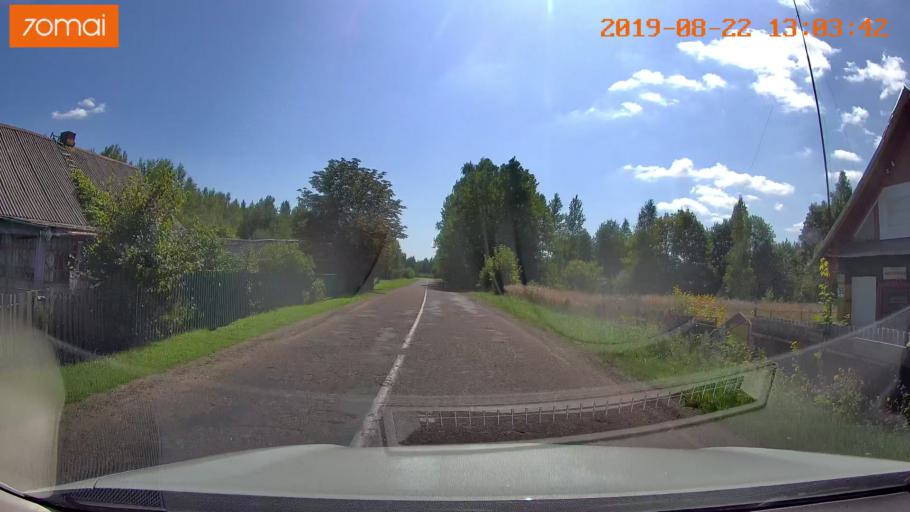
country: BY
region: Minsk
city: Prawdzinski
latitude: 53.3780
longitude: 27.8214
